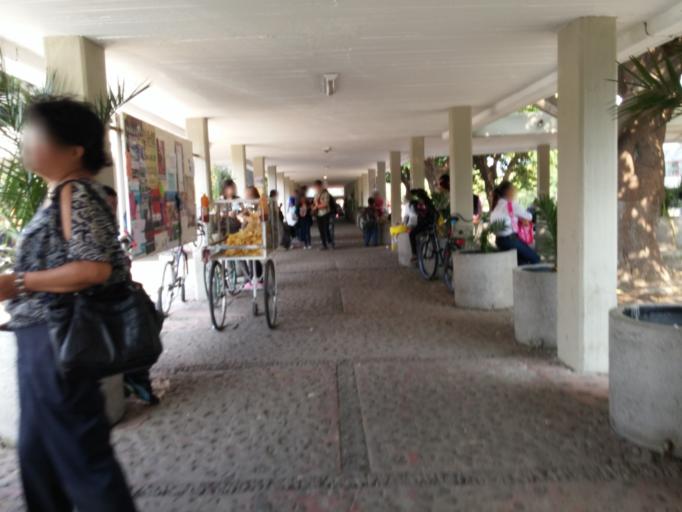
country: MX
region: Mexico City
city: Magdalena Contreras
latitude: 19.3338
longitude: -99.1875
